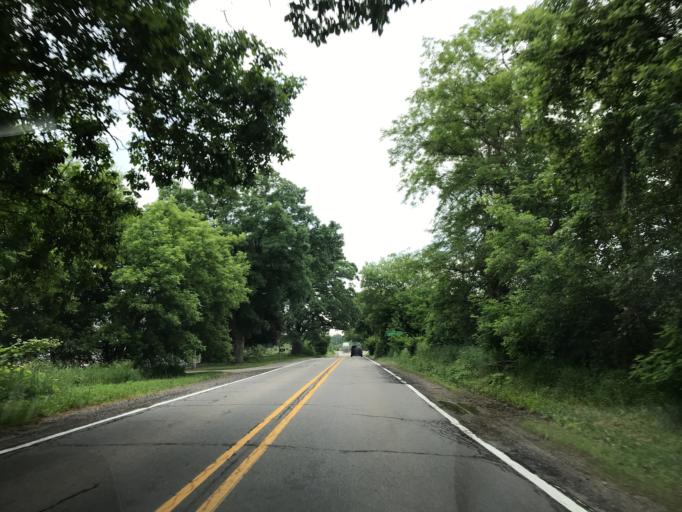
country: US
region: Michigan
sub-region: Oakland County
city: South Lyon
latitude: 42.5037
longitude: -83.6628
